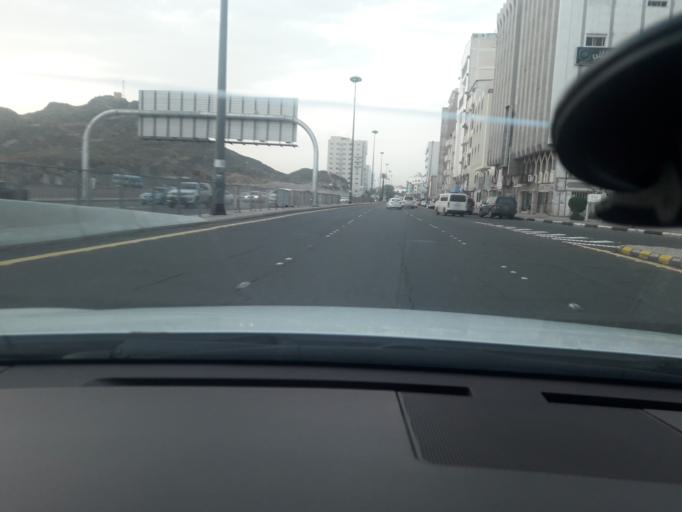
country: SA
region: Al Madinah al Munawwarah
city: Medina
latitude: 24.4765
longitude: 39.6046
